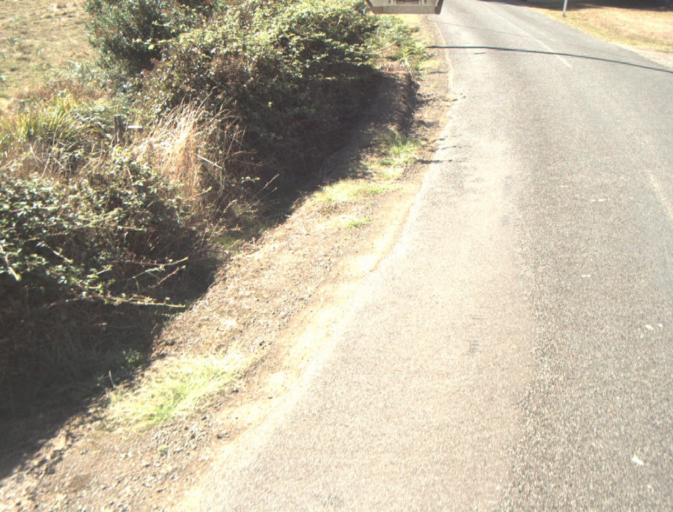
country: AU
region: Tasmania
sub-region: Launceston
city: Mayfield
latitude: -41.2942
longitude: 147.2040
